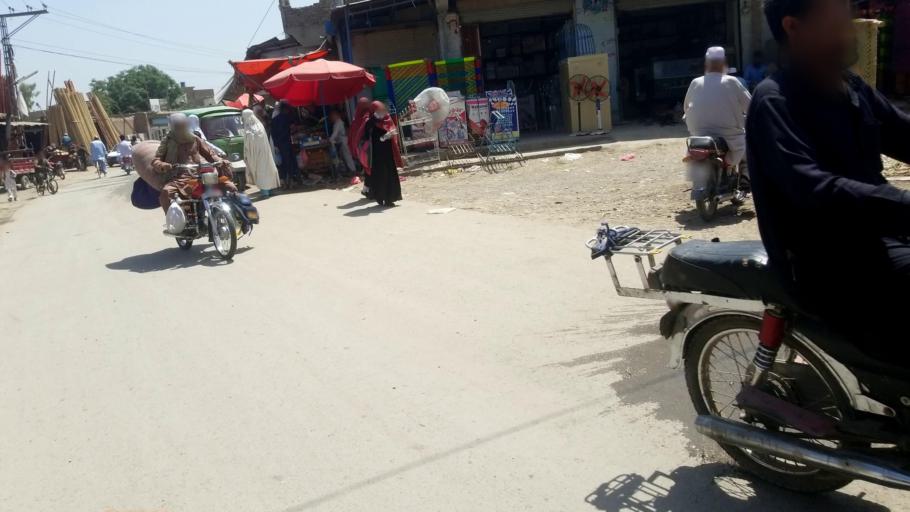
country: PK
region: Khyber Pakhtunkhwa
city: Peshawar
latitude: 34.0293
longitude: 71.4878
